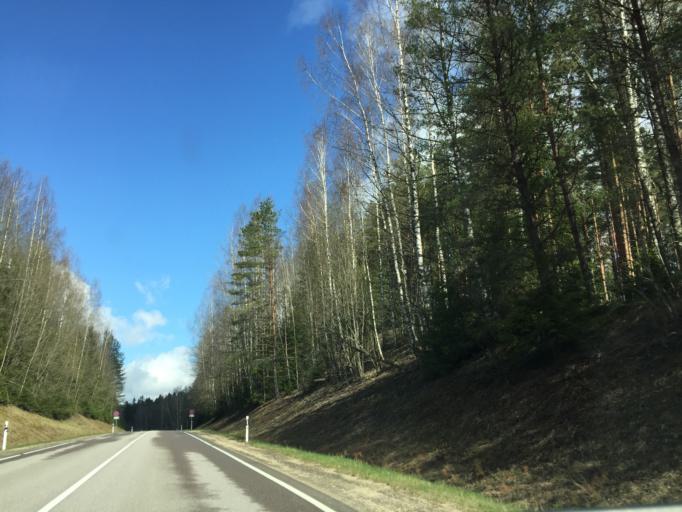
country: LV
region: Apes Novads
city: Ape
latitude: 57.5205
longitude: 26.7626
